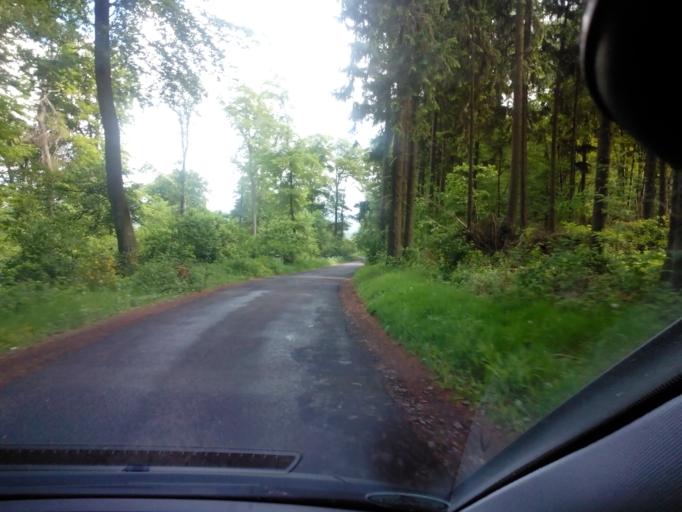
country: DE
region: Saarland
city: Schmelz
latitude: 49.3886
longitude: 6.8564
